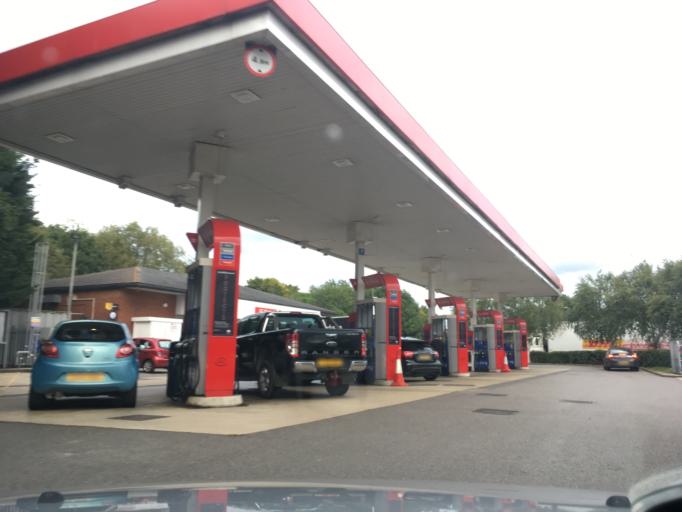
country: GB
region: England
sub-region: Oxfordshire
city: Banbury
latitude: 52.0692
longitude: -1.3165
